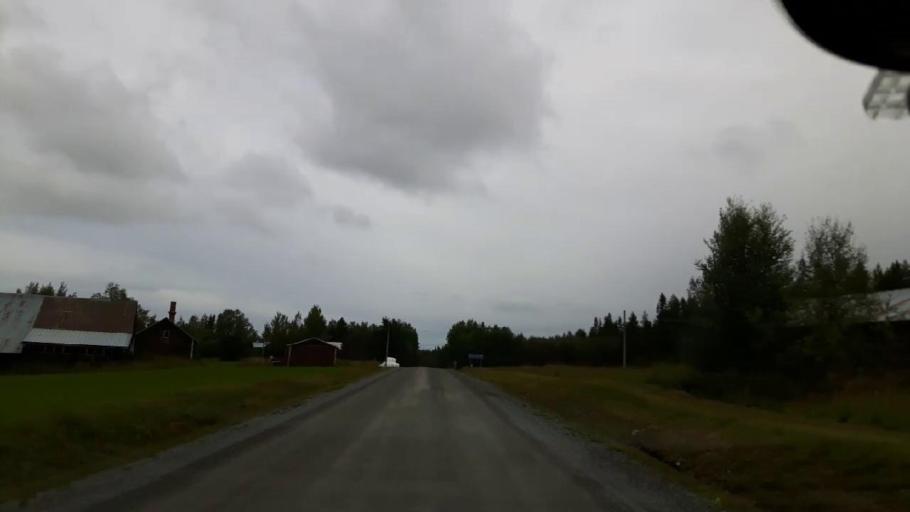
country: SE
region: Jaemtland
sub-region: OEstersunds Kommun
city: Ostersund
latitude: 63.1072
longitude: 14.5460
